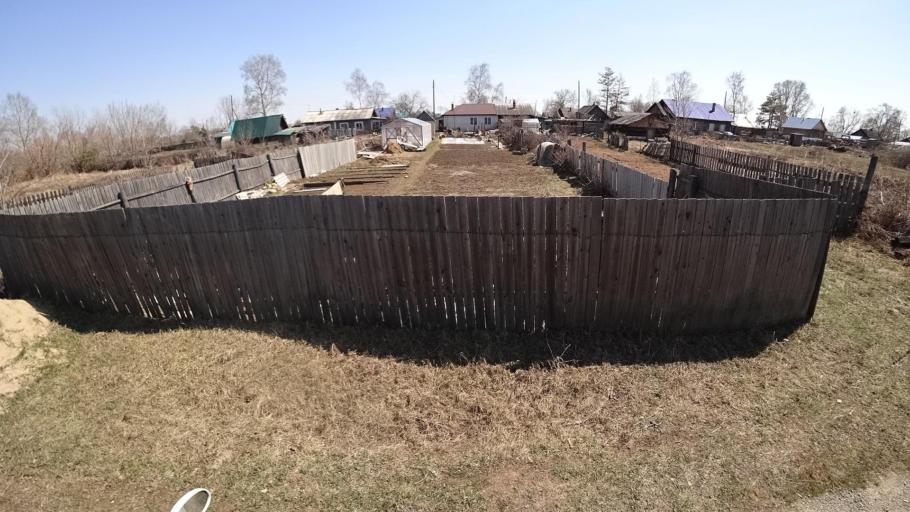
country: RU
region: Khabarovsk Krai
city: Khurba
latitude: 50.4092
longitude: 136.8832
